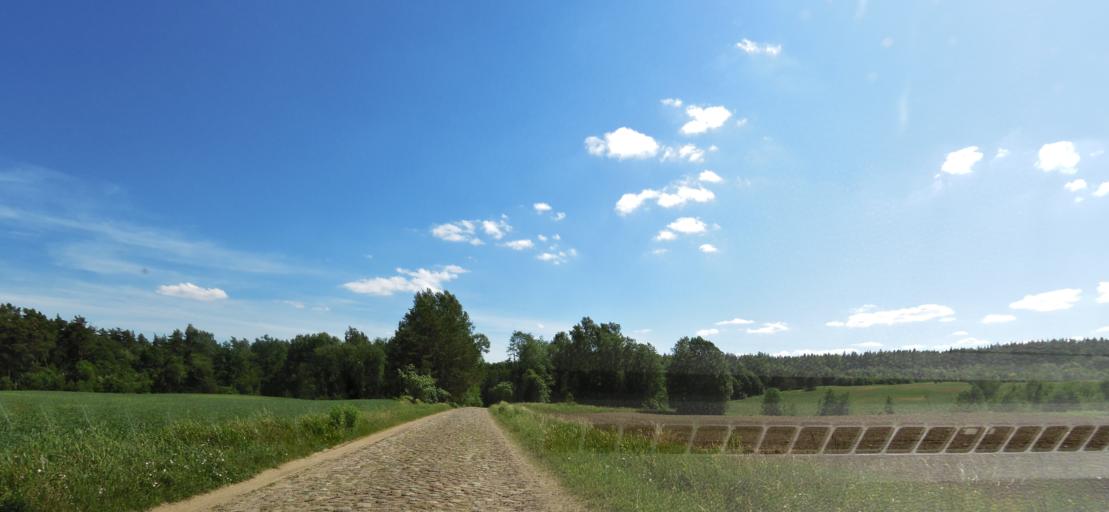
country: LT
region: Vilnius County
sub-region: Vilnius
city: Fabijoniskes
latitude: 54.8321
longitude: 25.3243
